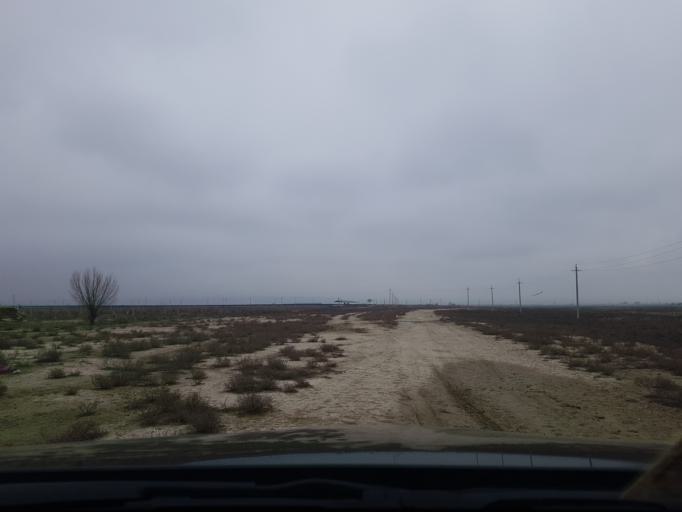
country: TM
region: Ahal
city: Abadan
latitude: 38.1432
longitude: 57.9802
